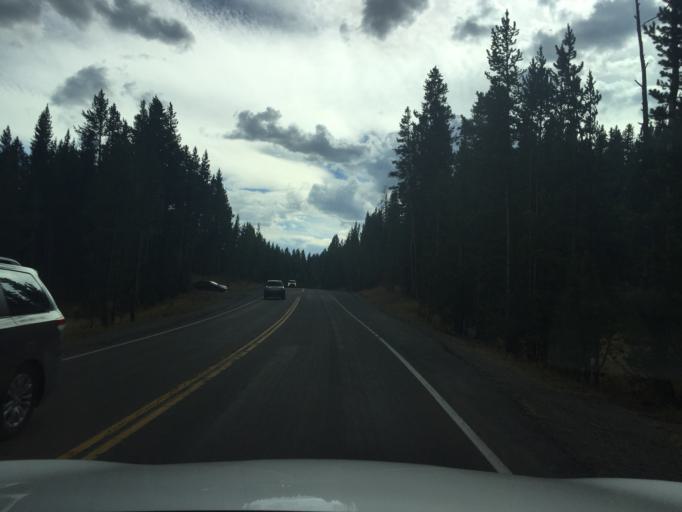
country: US
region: Montana
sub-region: Gallatin County
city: West Yellowstone
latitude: 44.7179
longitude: -110.5047
